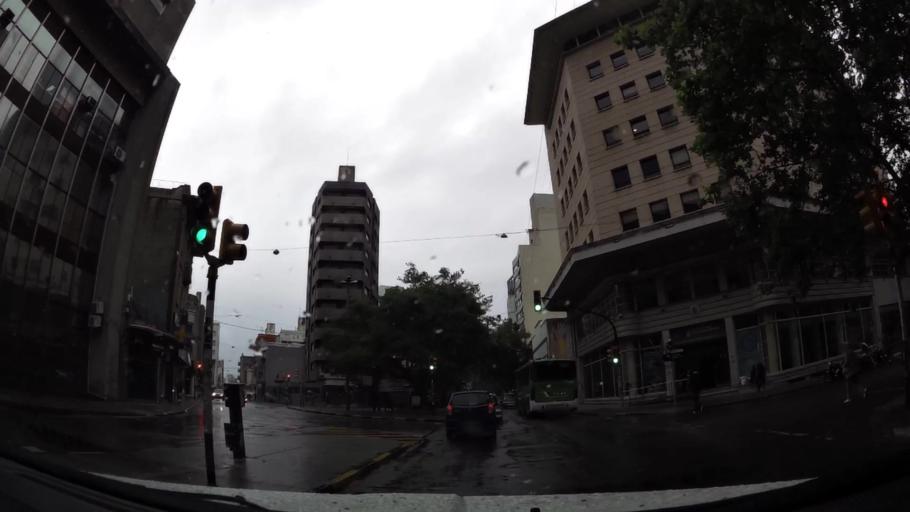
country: UY
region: Montevideo
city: Montevideo
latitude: -34.9058
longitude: -56.1834
